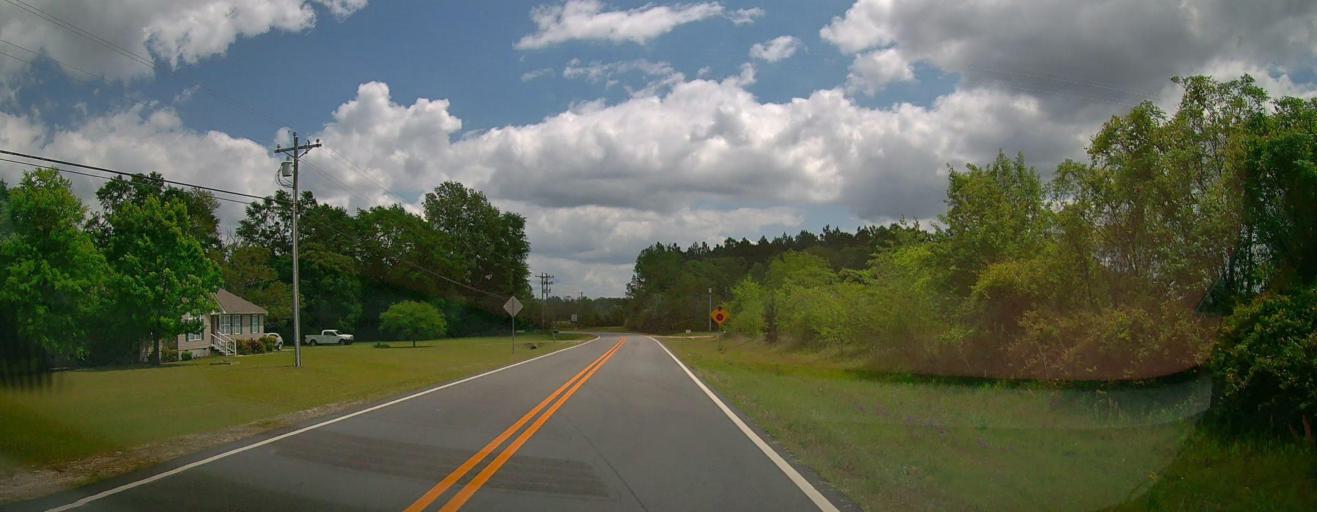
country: US
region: Georgia
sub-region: Laurens County
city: Dublin
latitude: 32.6003
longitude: -82.9596
